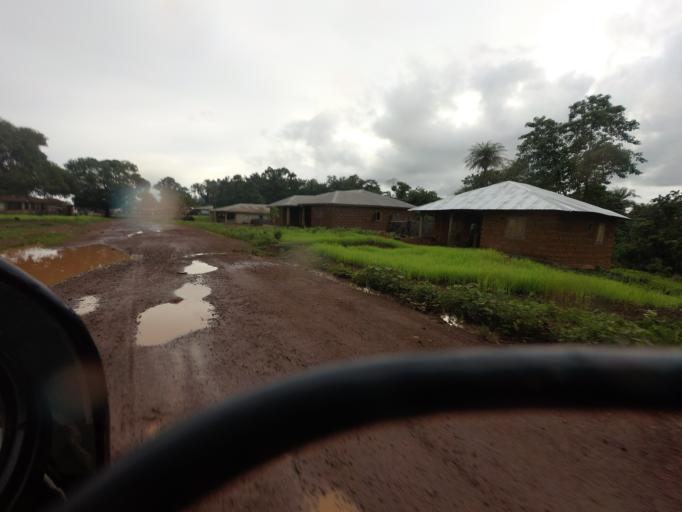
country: SL
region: Northern Province
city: Kambia
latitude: 9.2389
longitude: -12.7999
